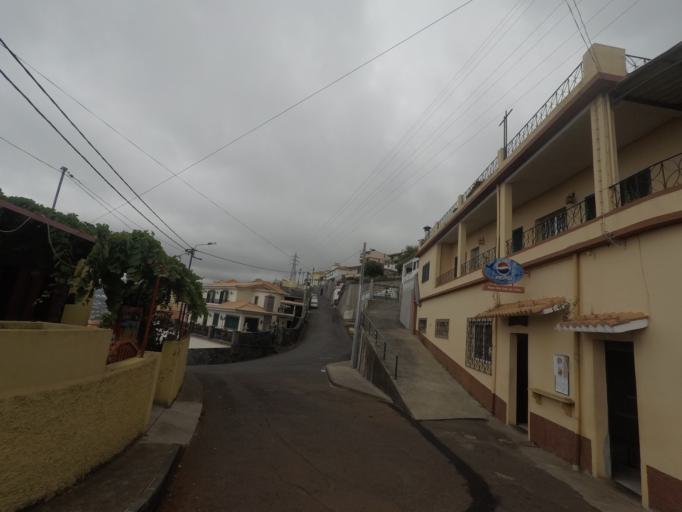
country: PT
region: Madeira
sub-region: Funchal
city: Nossa Senhora do Monte
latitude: 32.6665
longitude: -16.8900
